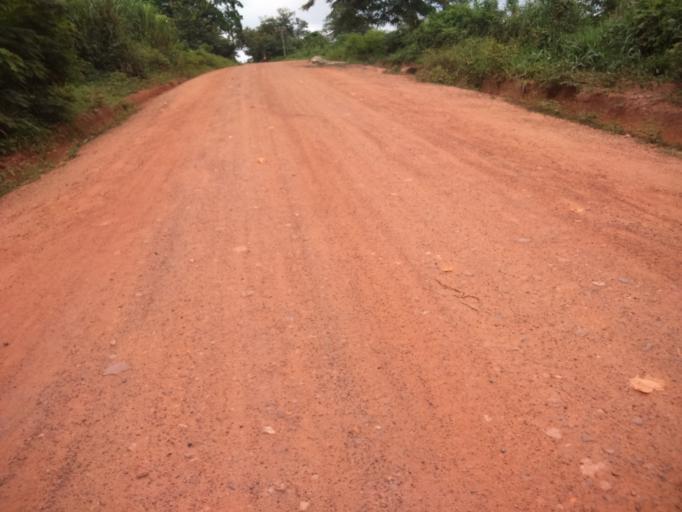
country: CI
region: Lagunes
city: Agou
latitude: 6.0883
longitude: -4.0654
